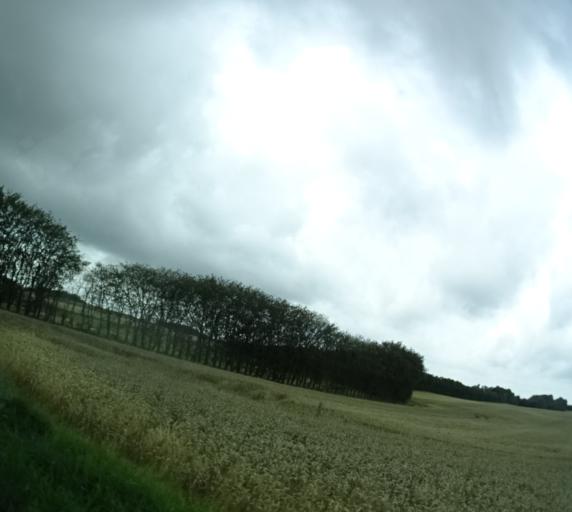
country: DK
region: Central Jutland
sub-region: Syddjurs Kommune
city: Ryomgard
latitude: 56.3900
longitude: 10.5513
